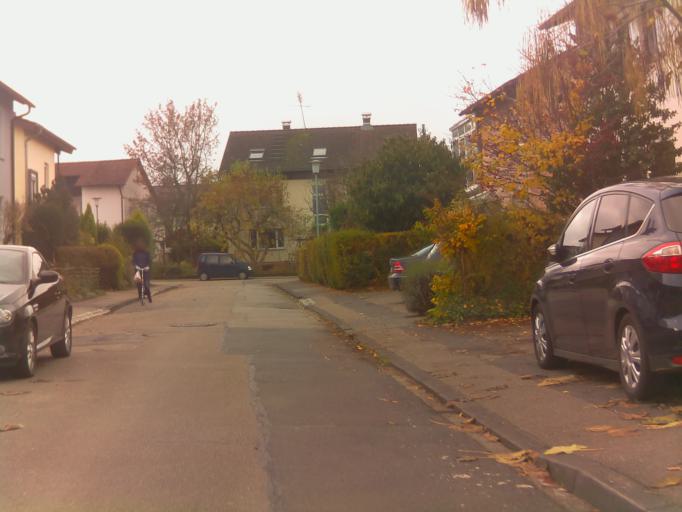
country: DE
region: Baden-Wuerttemberg
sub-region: Karlsruhe Region
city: Weinheim
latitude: 49.5467
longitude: 8.6465
